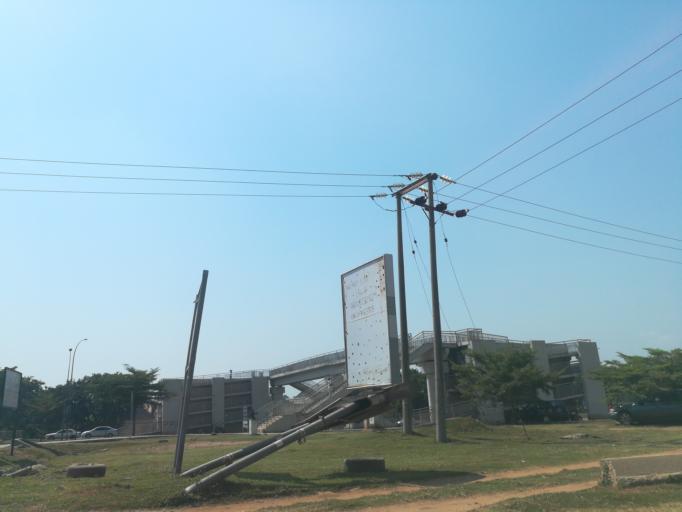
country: NG
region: Abuja Federal Capital Territory
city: Abuja
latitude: 9.0792
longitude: 7.4501
